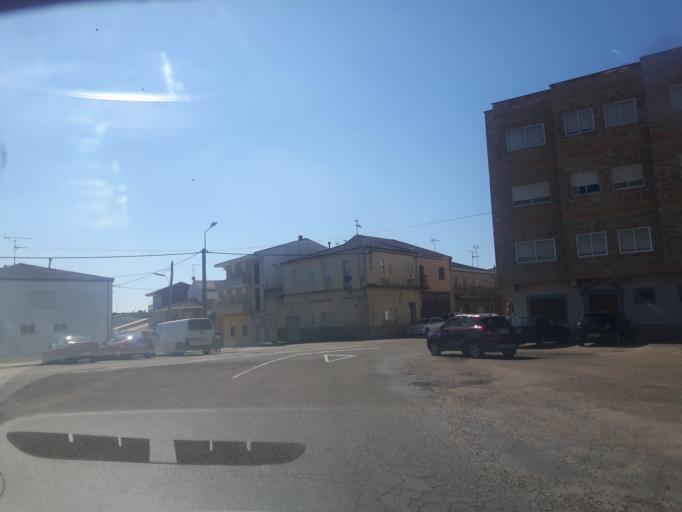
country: ES
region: Castille and Leon
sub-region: Provincia de Salamanca
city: Vitigudino
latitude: 41.0123
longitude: -6.4345
